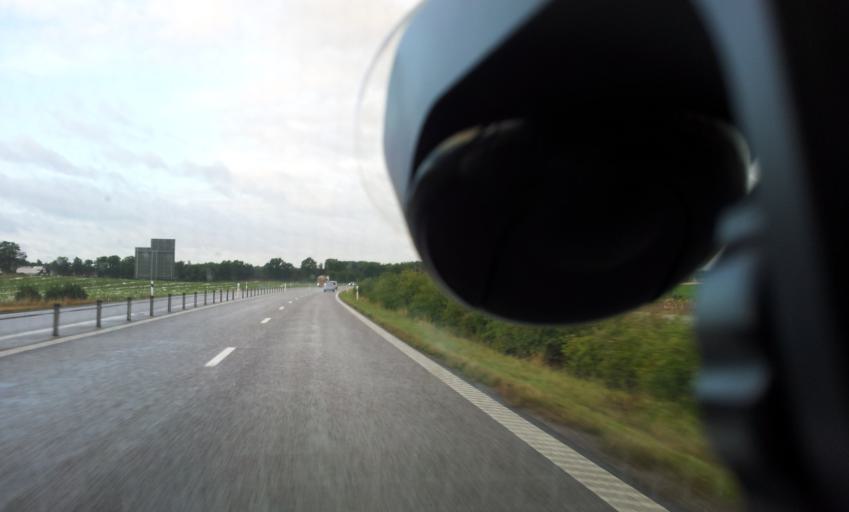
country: SE
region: Kalmar
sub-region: Kalmar Kommun
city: Lindsdal
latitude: 56.7869
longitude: 16.3443
